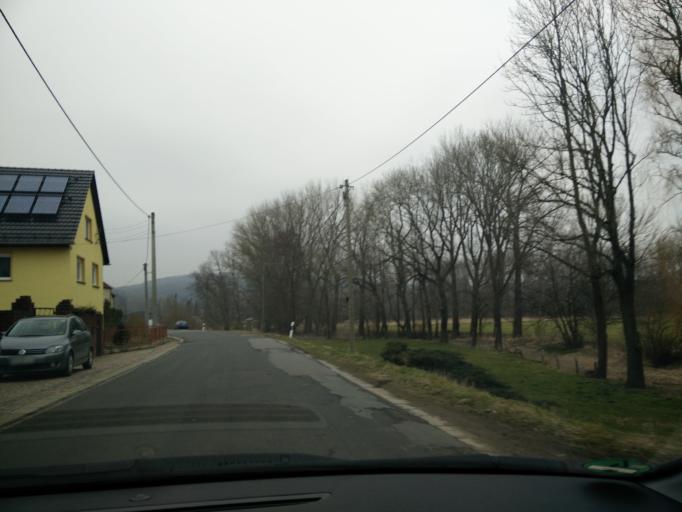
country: DE
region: Saxony
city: Wechselburg
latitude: 50.9973
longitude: 12.7698
